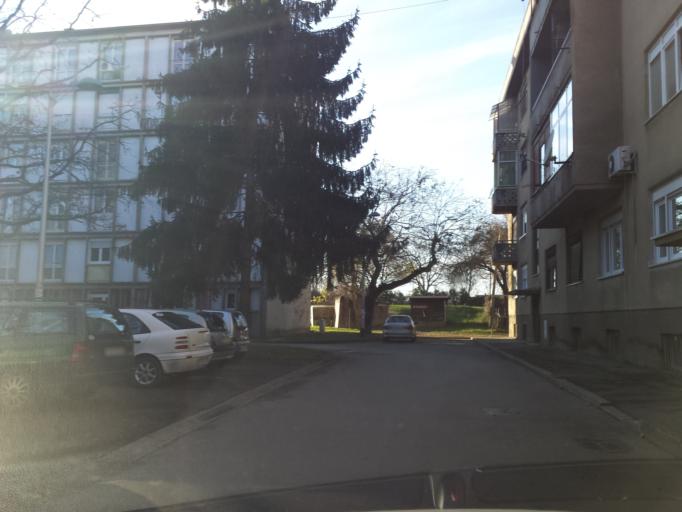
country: HR
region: Grad Zagreb
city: Jankomir
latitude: 45.8025
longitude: 15.9263
